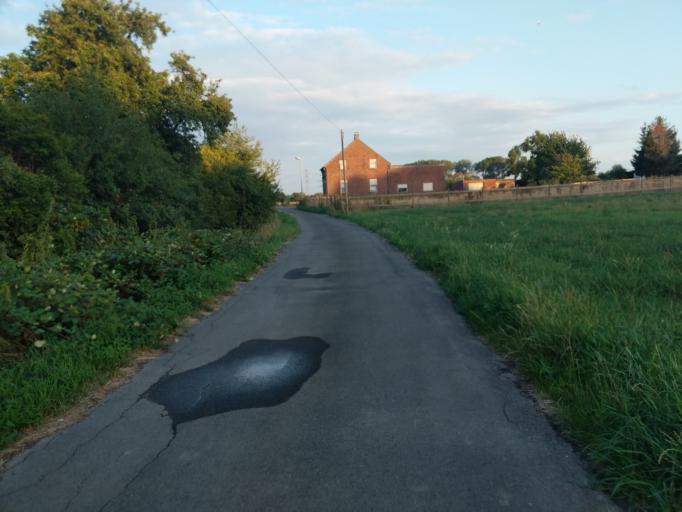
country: DE
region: North Rhine-Westphalia
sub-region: Regierungsbezirk Dusseldorf
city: Meerbusch
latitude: 51.3254
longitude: 6.6660
